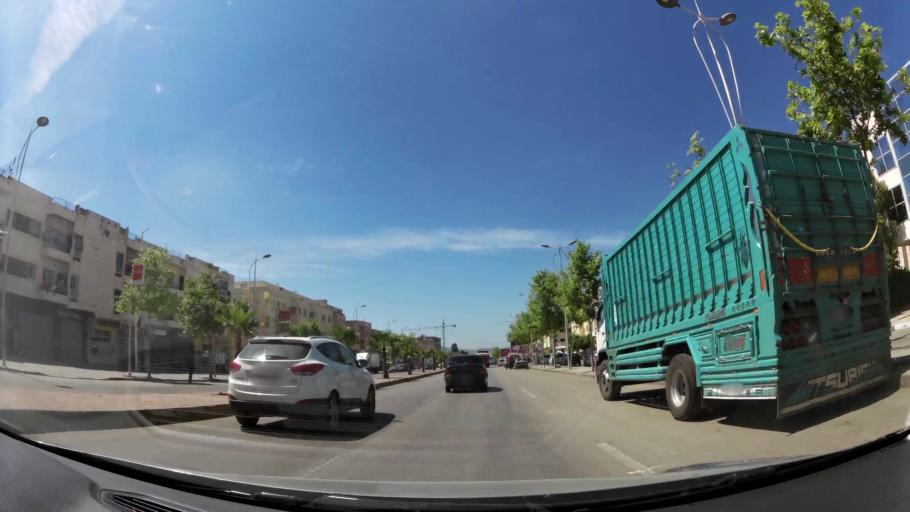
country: MA
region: Fes-Boulemane
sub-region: Fes
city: Fes
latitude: 34.0085
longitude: -4.9783
